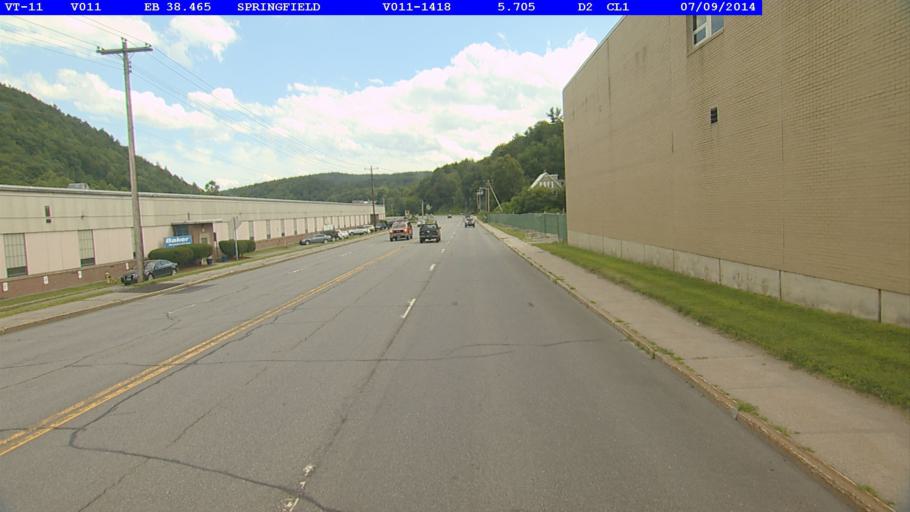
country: US
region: Vermont
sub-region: Windsor County
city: Springfield
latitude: 43.2861
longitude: -72.4716
